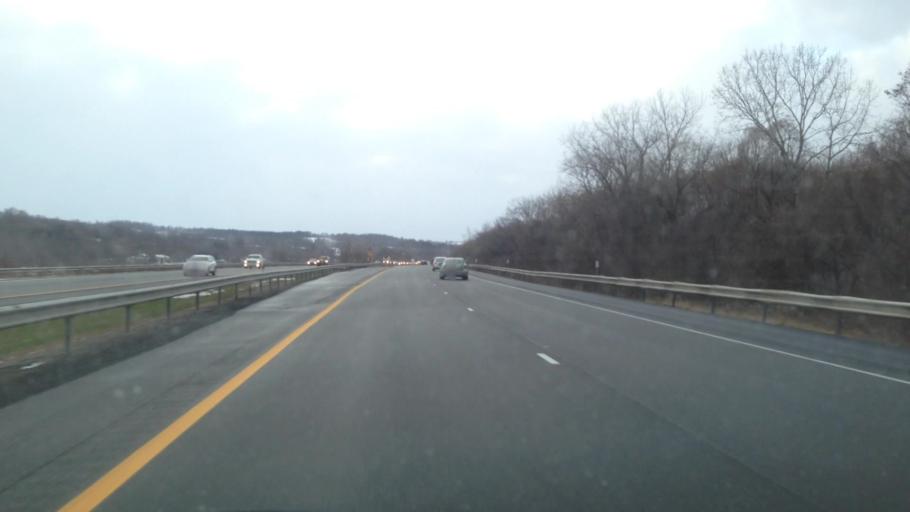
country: US
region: New York
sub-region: Montgomery County
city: Canajoharie
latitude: 42.8940
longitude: -74.5008
